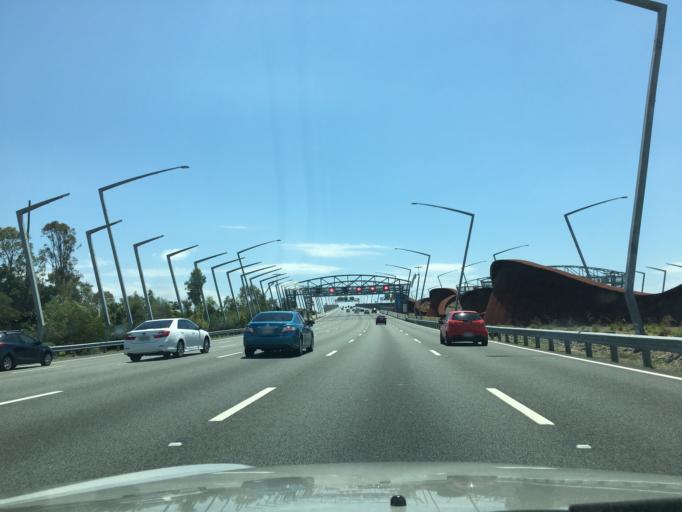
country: AU
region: Queensland
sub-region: Brisbane
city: Cannon Hill
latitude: -27.4527
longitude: 153.1050
